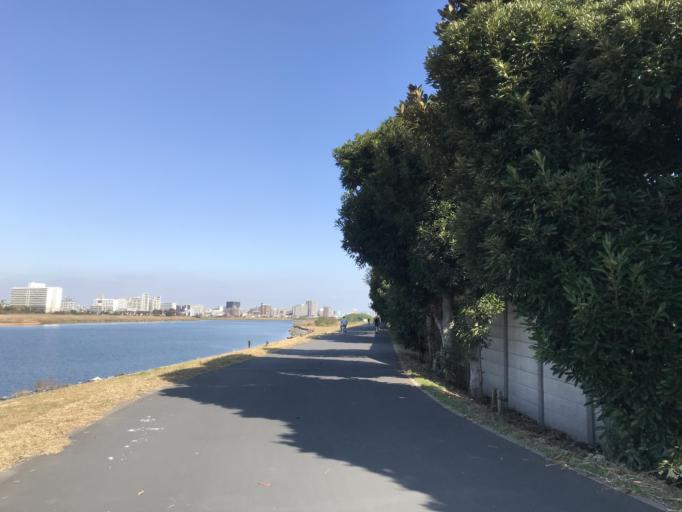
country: JP
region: Kanagawa
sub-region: Kawasaki-shi
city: Kawasaki
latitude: 35.5367
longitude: 139.7192
